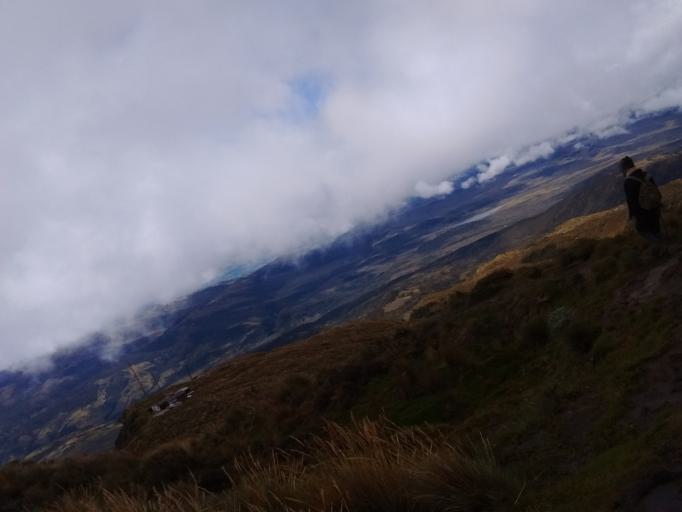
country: CO
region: Cauca
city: Totoro
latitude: 2.3319
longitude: -76.3944
